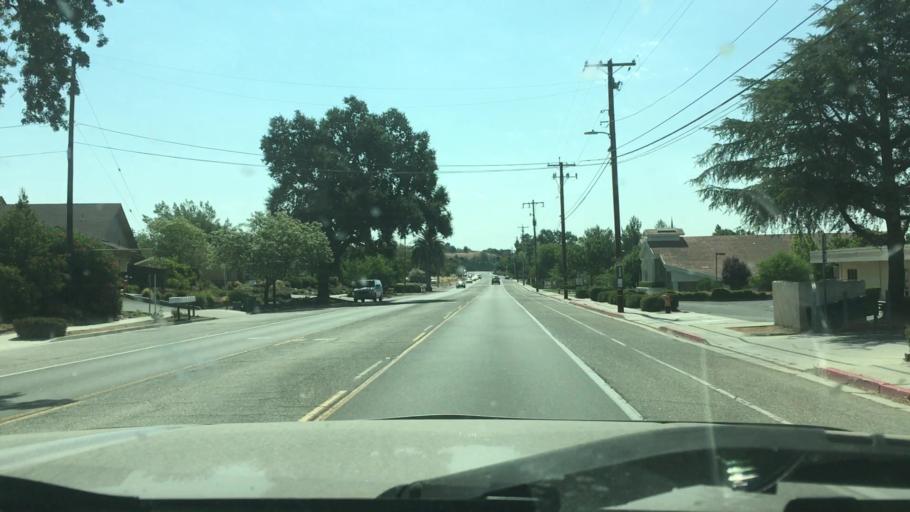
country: US
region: California
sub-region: San Luis Obispo County
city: Paso Robles
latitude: 35.6247
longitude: -120.6688
